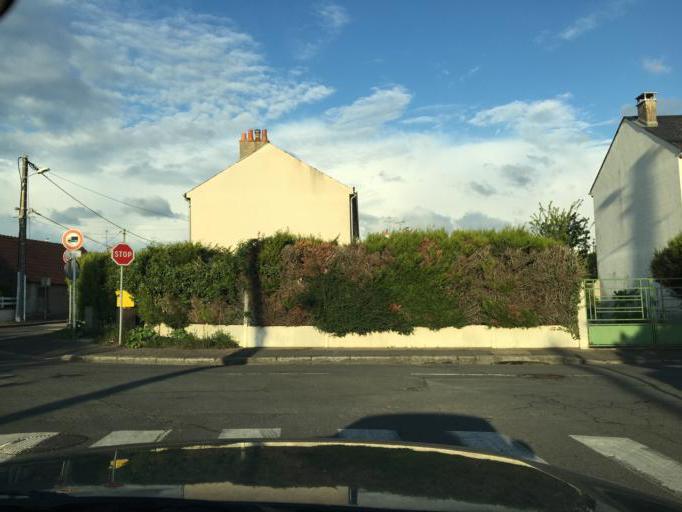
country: FR
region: Centre
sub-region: Departement du Loiret
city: Semoy
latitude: 47.9203
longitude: 1.9375
